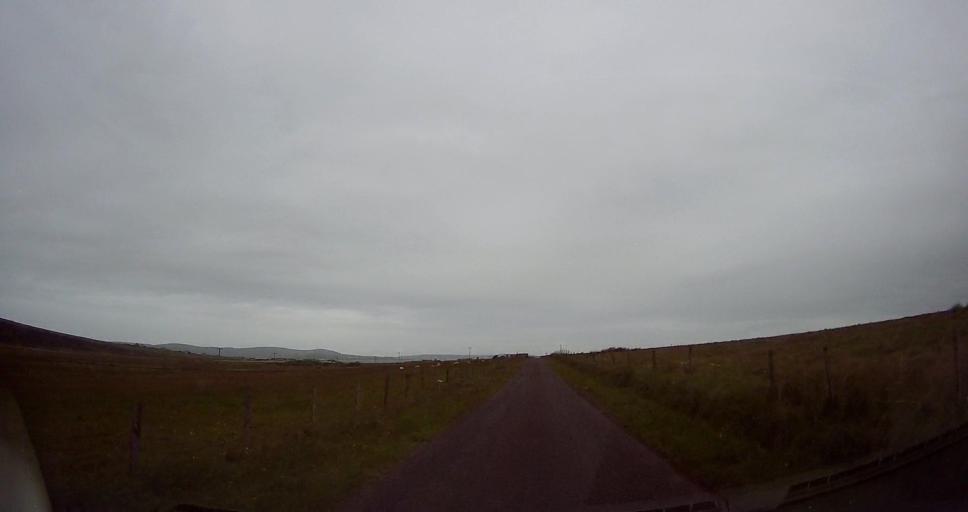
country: GB
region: Scotland
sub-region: Orkney Islands
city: Stromness
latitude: 58.9819
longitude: -3.1814
